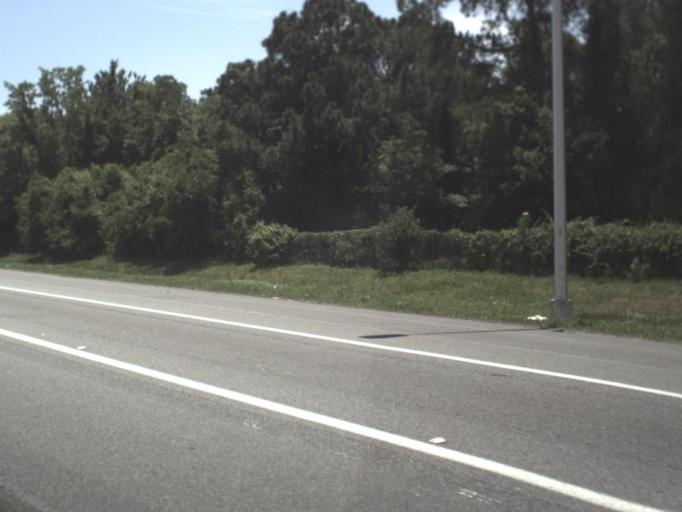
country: US
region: Florida
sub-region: Clay County
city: Bellair-Meadowbrook Terrace
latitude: 30.2151
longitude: -81.7609
